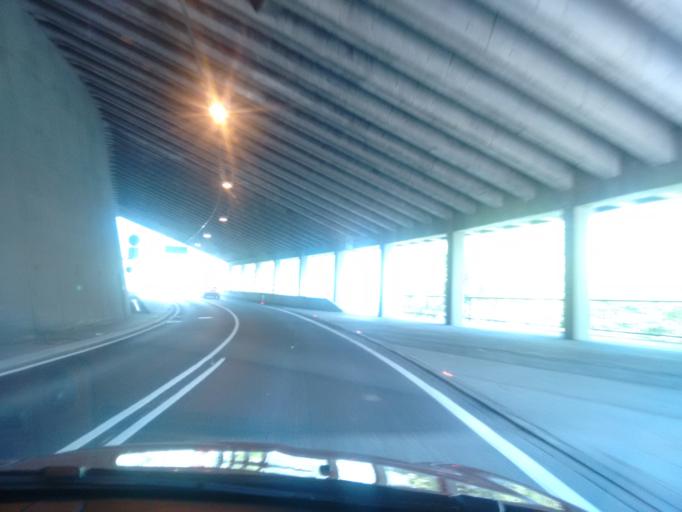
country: AT
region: Upper Austria
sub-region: Politischer Bezirk Gmunden
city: Ebensee
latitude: 47.8266
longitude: 13.7887
